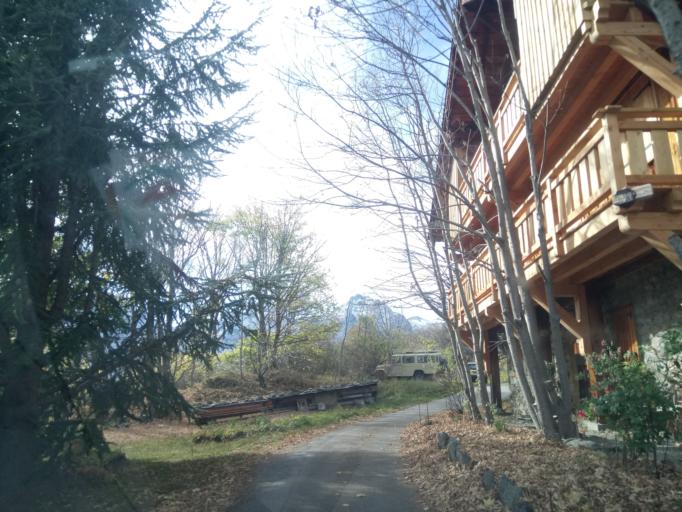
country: FR
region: Rhone-Alpes
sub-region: Departement de la Savoie
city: La Chambre
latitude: 45.3852
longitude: 6.3046
